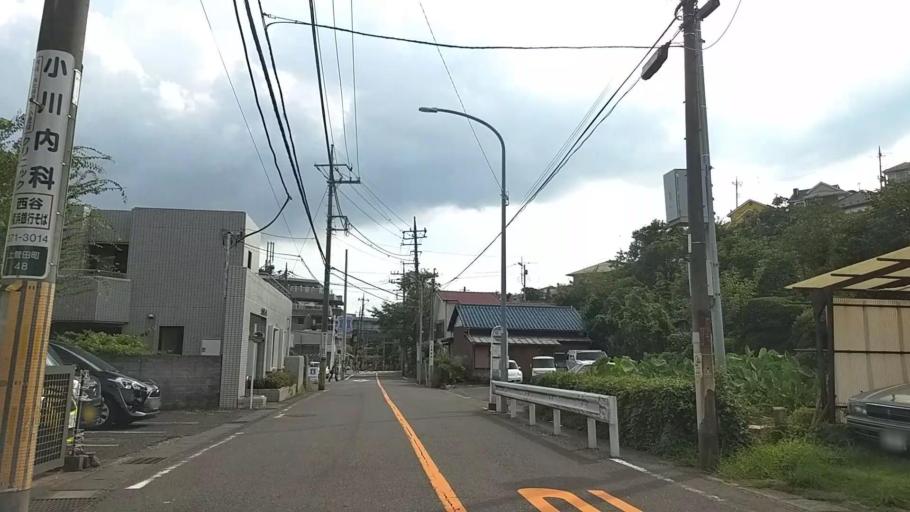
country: JP
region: Kanagawa
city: Yokohama
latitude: 35.4816
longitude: 139.5706
